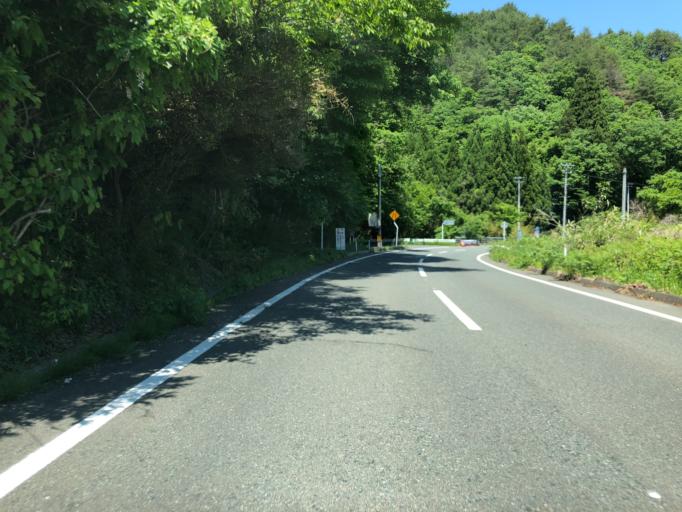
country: JP
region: Fukushima
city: Namie
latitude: 37.5179
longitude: 140.8489
